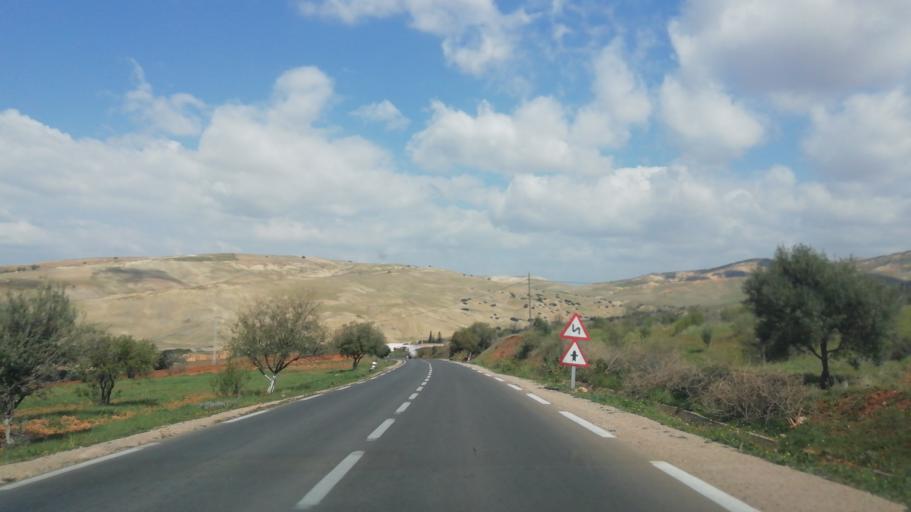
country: DZ
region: Mascara
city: Mascara
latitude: 35.5353
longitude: 0.1121
